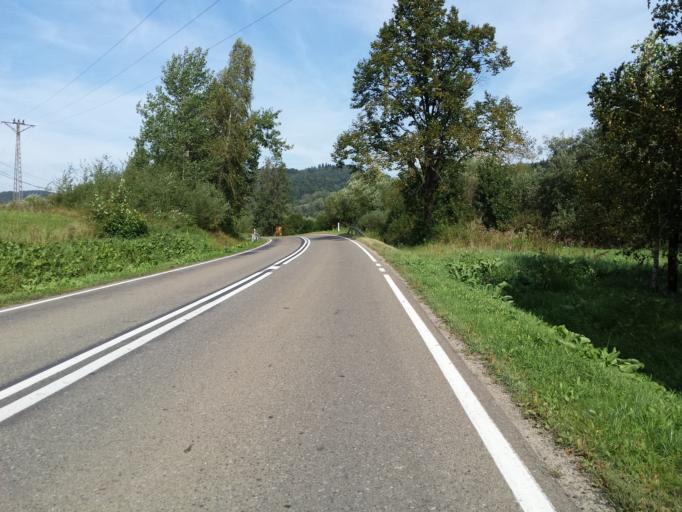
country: PL
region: Subcarpathian Voivodeship
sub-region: Powiat leski
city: Baligrod
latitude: 49.3500
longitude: 22.2892
